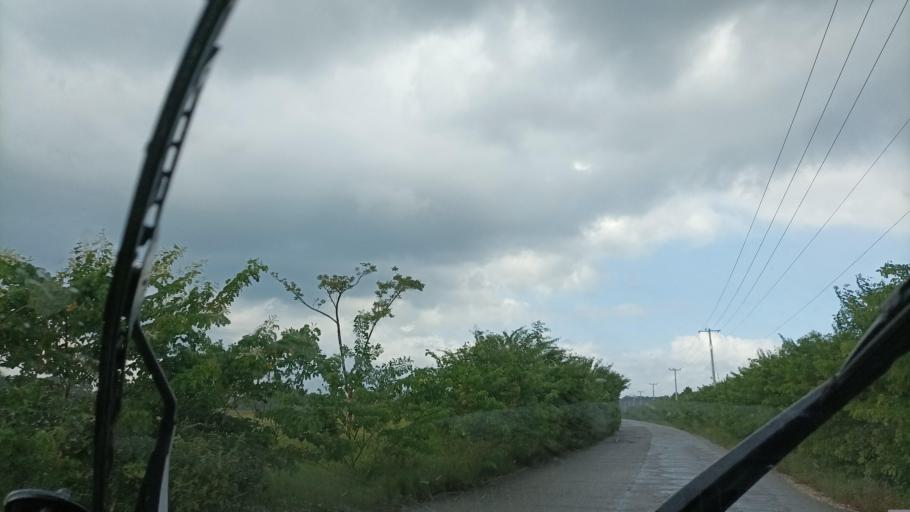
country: MX
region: Veracruz
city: Las Choapas
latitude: 17.8410
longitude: -94.1041
